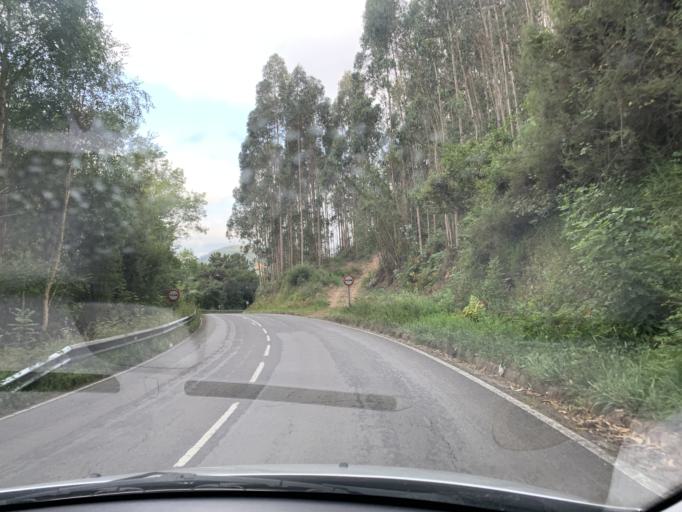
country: ES
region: Asturias
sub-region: Province of Asturias
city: Villaviciosa
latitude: 43.5109
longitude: -5.4272
